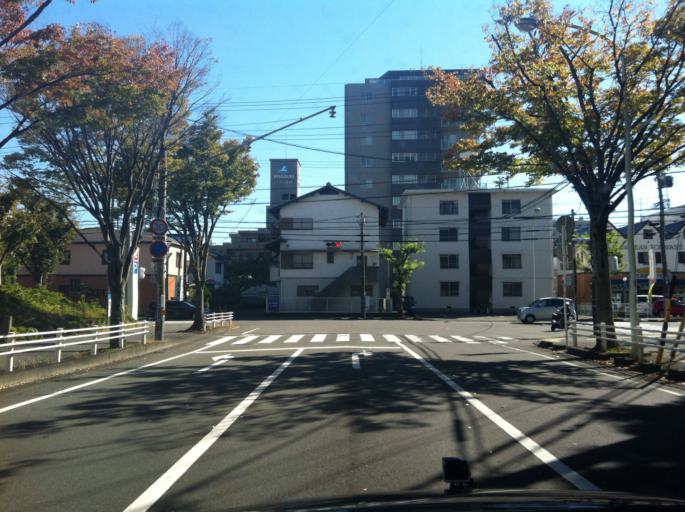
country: JP
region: Shizuoka
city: Shizuoka-shi
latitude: 34.9713
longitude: 138.4073
